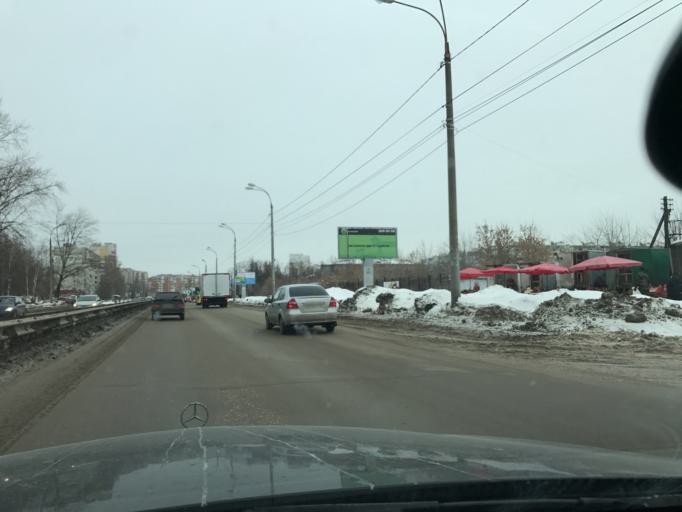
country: RU
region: Nizjnij Novgorod
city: Gorbatovka
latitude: 56.2509
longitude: 43.8518
